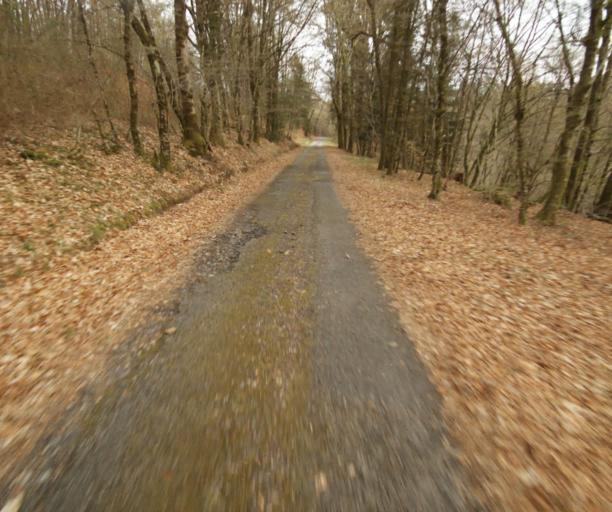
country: FR
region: Limousin
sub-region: Departement de la Correze
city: Argentat
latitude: 45.2088
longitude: 1.9907
